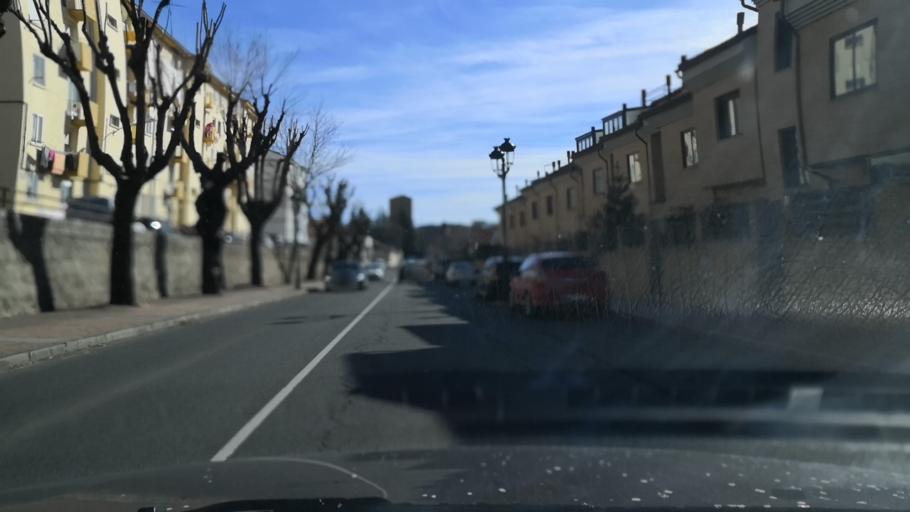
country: ES
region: Castille and Leon
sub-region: Provincia de Avila
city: Avila
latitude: 40.6532
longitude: -4.7048
